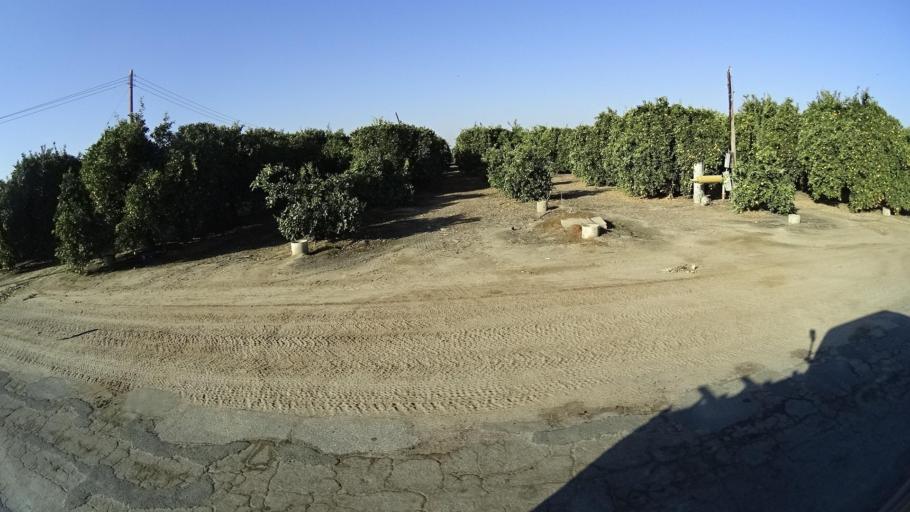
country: US
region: California
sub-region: Tulare County
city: Richgrove
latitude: 35.7731
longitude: -119.1607
